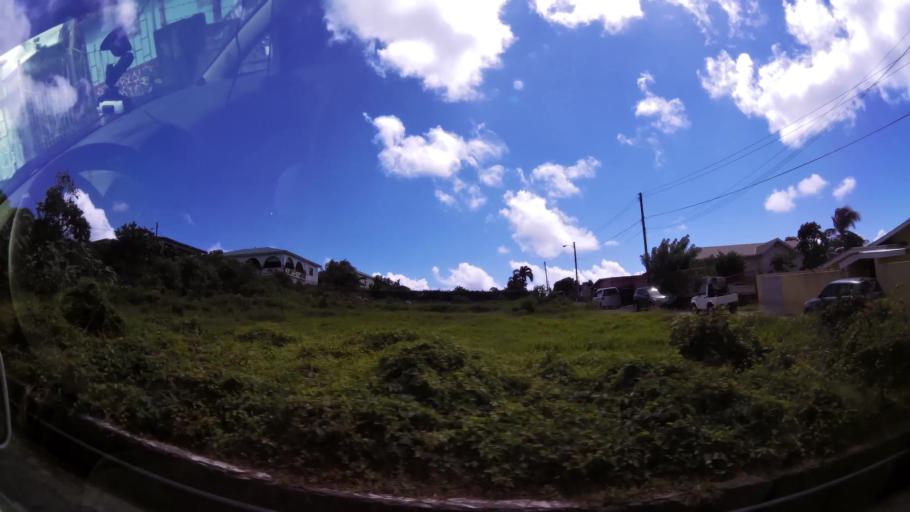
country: VC
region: Saint George
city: Kingstown
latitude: 13.1429
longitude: -61.2244
